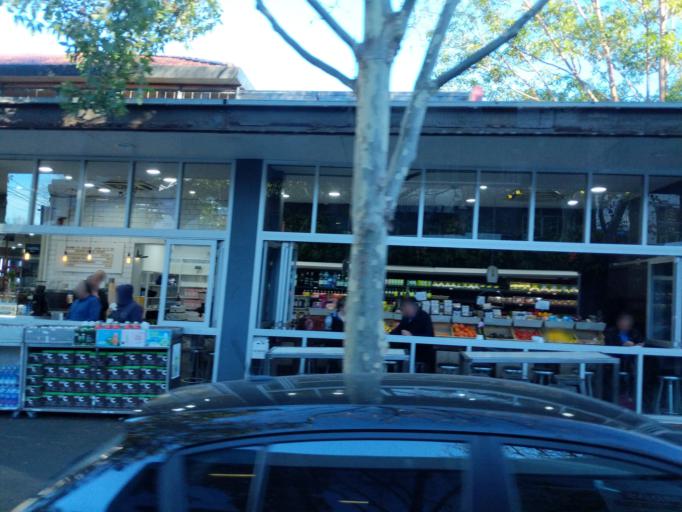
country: AU
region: New South Wales
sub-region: City of Sydney
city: Darlinghurst
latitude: -33.8849
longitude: 151.2141
